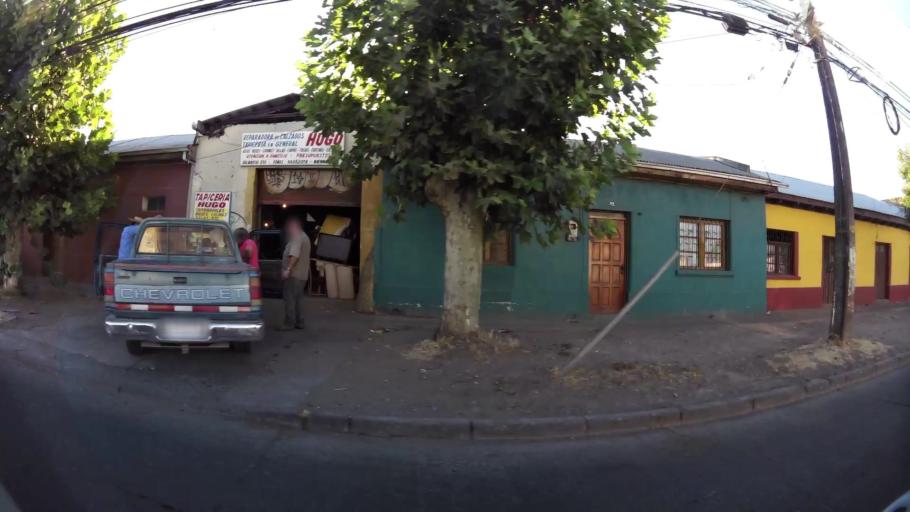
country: CL
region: Maule
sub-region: Provincia de Curico
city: Curico
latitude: -34.9812
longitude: -71.2479
